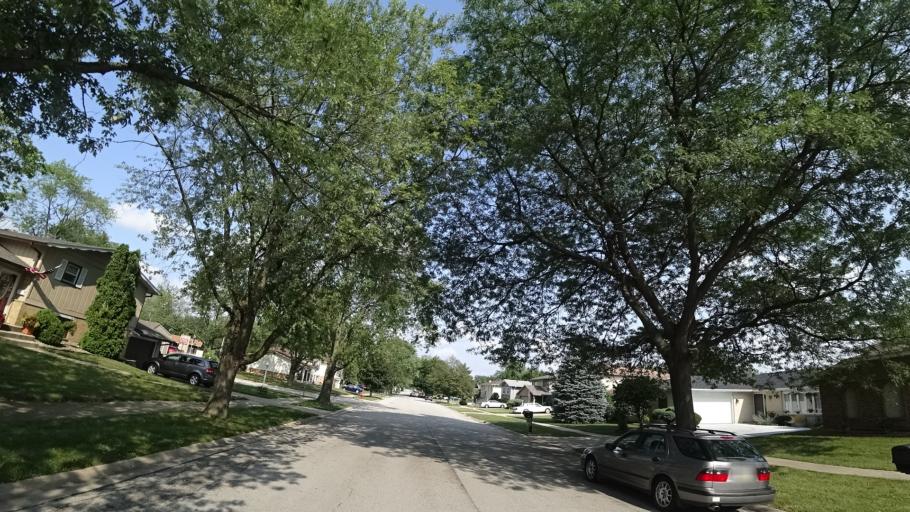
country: US
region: Illinois
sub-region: Cook County
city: Oak Forest
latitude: 41.6100
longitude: -87.7702
